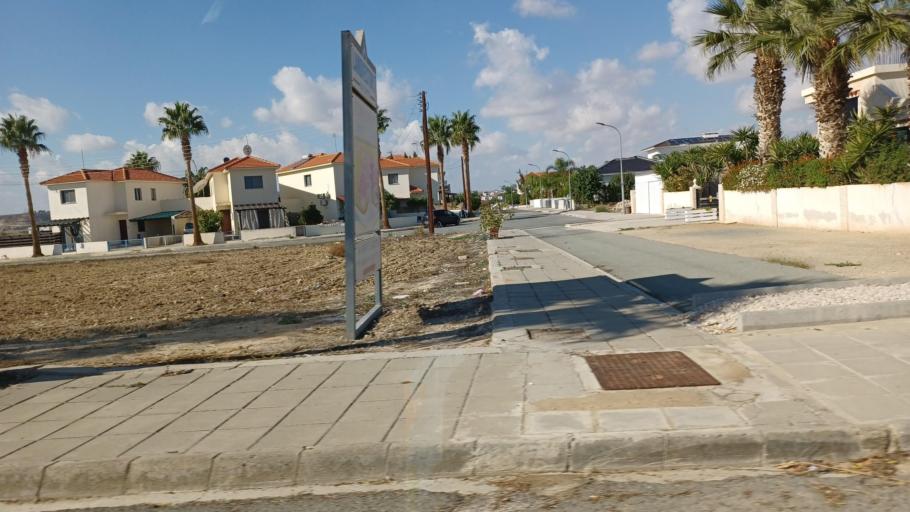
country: CY
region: Larnaka
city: Pyla
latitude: 34.9926
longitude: 33.6828
